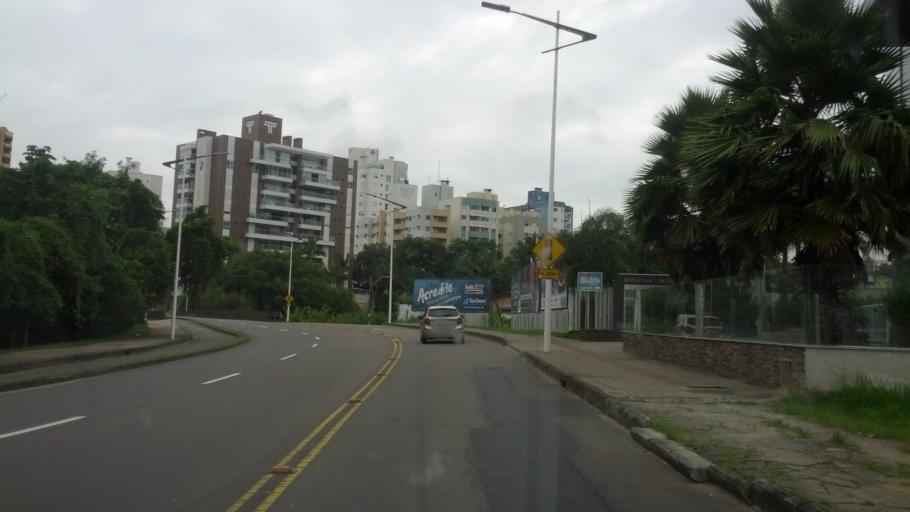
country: BR
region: Santa Catarina
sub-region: Blumenau
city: Blumenau
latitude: -26.9104
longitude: -49.0791
